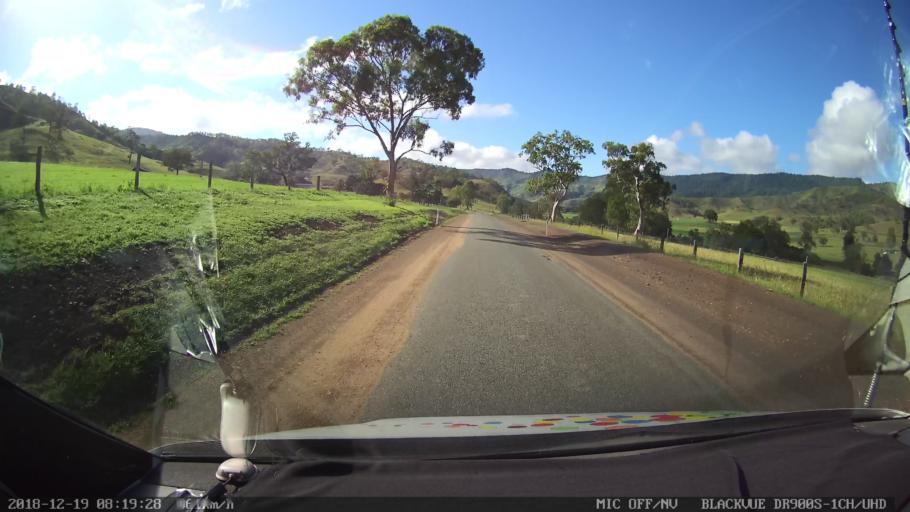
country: AU
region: New South Wales
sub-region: Kyogle
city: Kyogle
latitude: -28.2822
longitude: 152.9092
